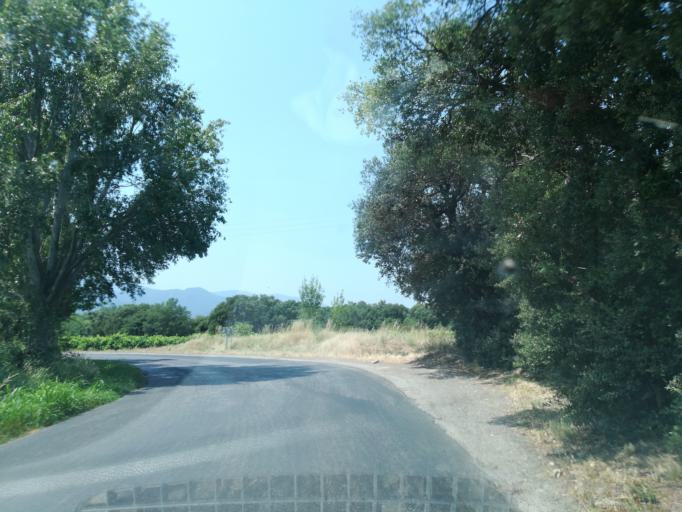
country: FR
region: Languedoc-Roussillon
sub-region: Departement des Pyrenees-Orientales
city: Sant Joan de Pladecorts
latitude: 42.5042
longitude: 2.7983
